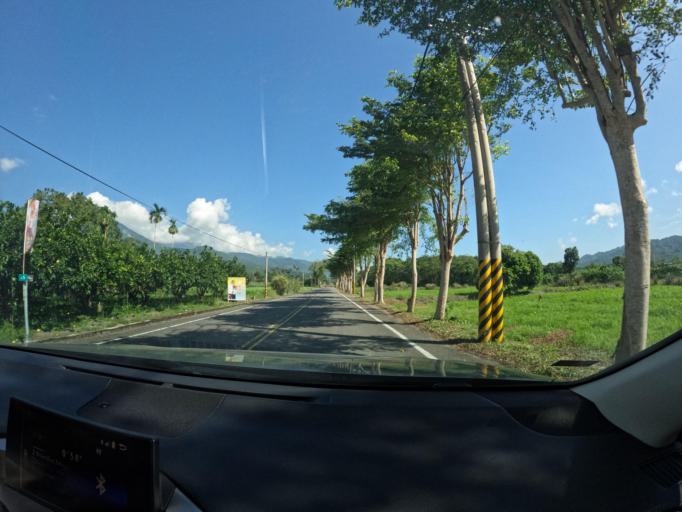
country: TW
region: Taiwan
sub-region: Hualien
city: Hualian
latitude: 23.5602
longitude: 121.3789
